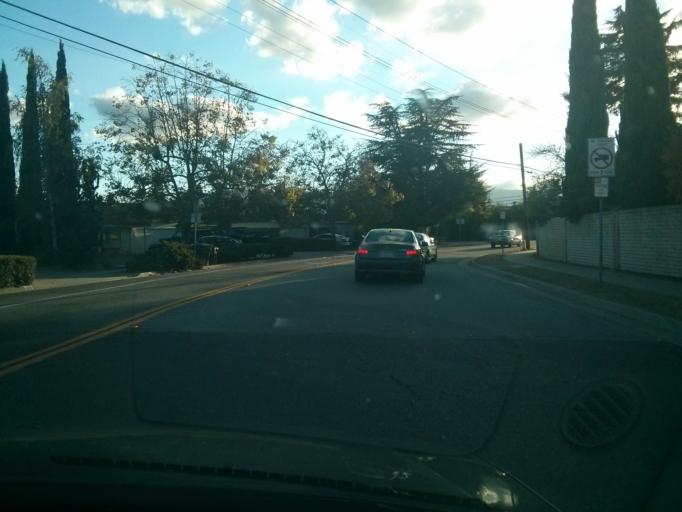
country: US
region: California
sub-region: Santa Clara County
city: Campbell
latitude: 37.2796
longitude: -121.9576
